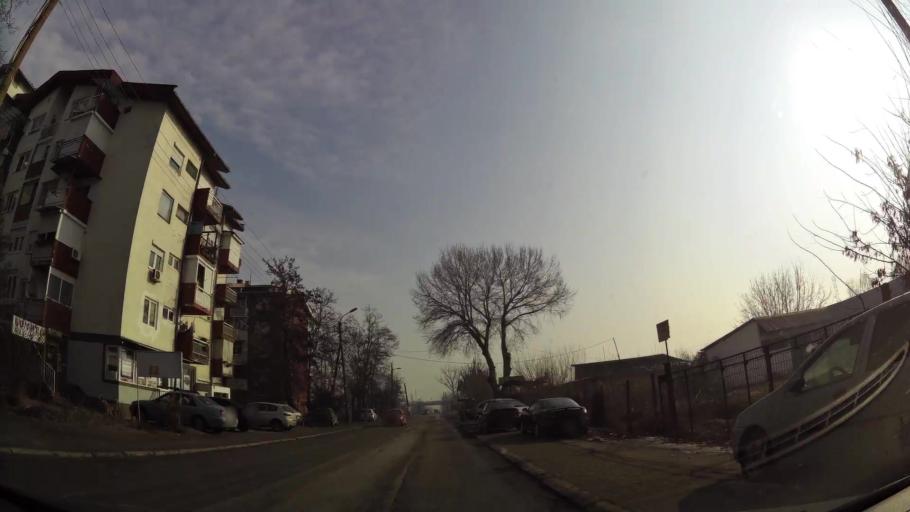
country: MK
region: Kisela Voda
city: Kisela Voda
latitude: 41.9919
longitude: 21.5087
